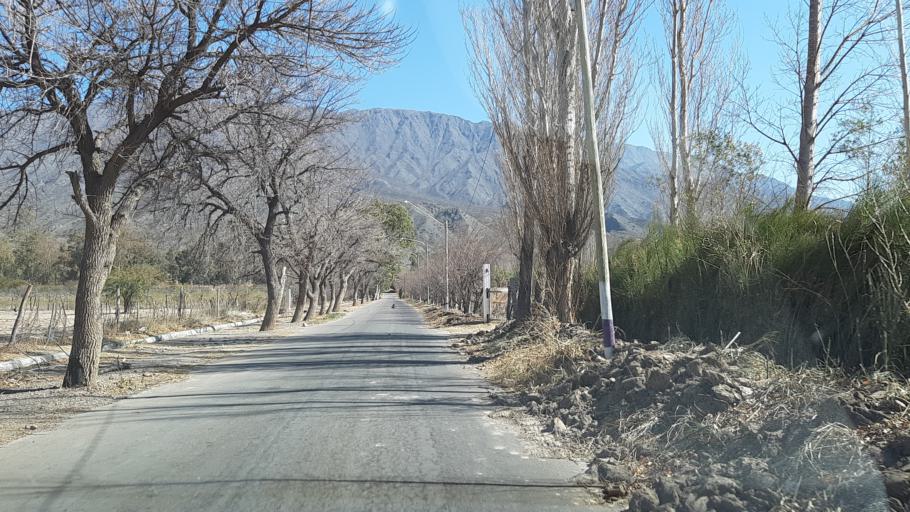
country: AR
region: San Juan
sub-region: Departamento de Zonda
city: Zonda
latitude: -31.5713
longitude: -68.7527
